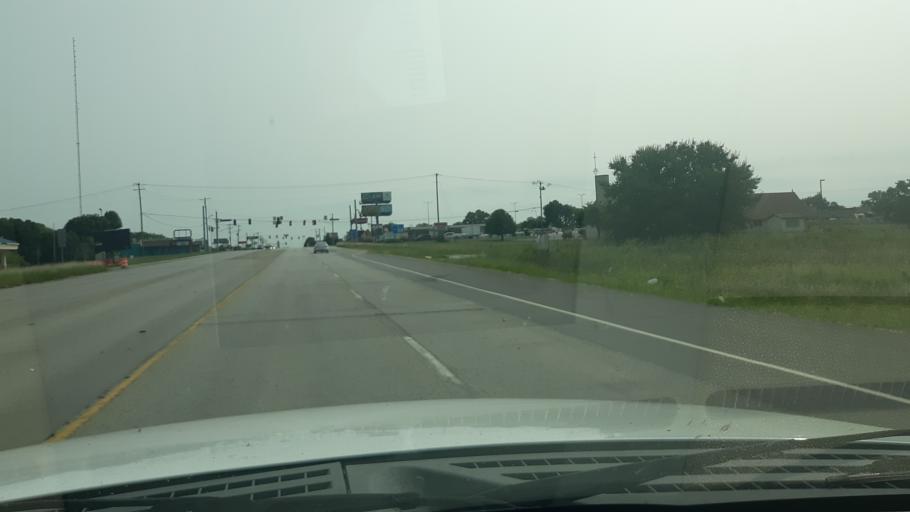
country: US
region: Indiana
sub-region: Gibson County
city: Princeton
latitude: 38.3555
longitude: -87.5962
